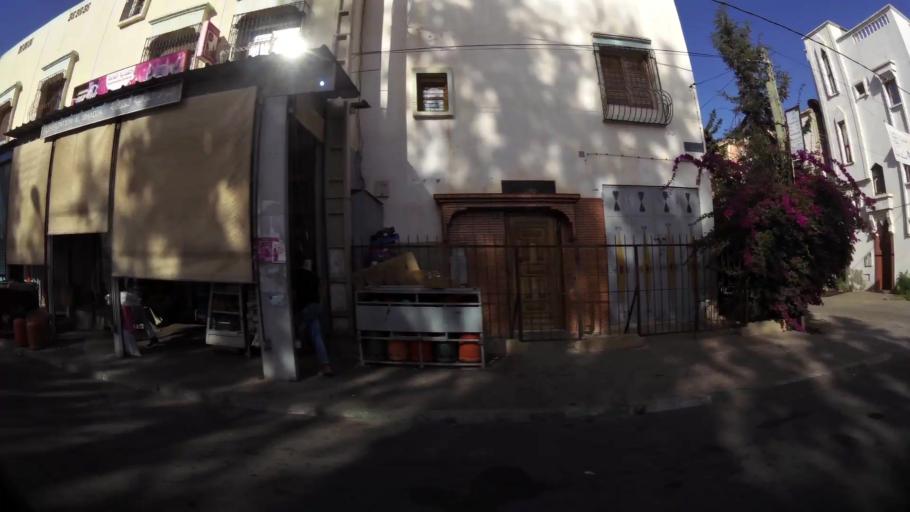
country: MA
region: Souss-Massa-Draa
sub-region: Inezgane-Ait Mellou
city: Inezgane
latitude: 30.3662
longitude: -9.5282
